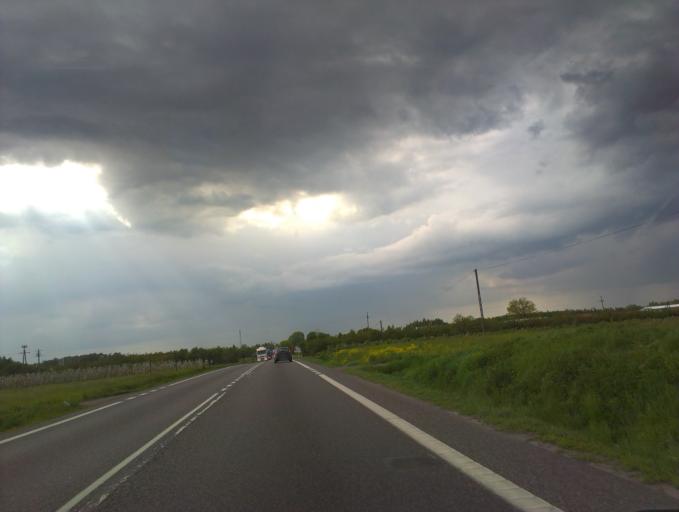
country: PL
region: Masovian Voivodeship
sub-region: Powiat grojecki
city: Pniewy
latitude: 51.9048
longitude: 20.7536
